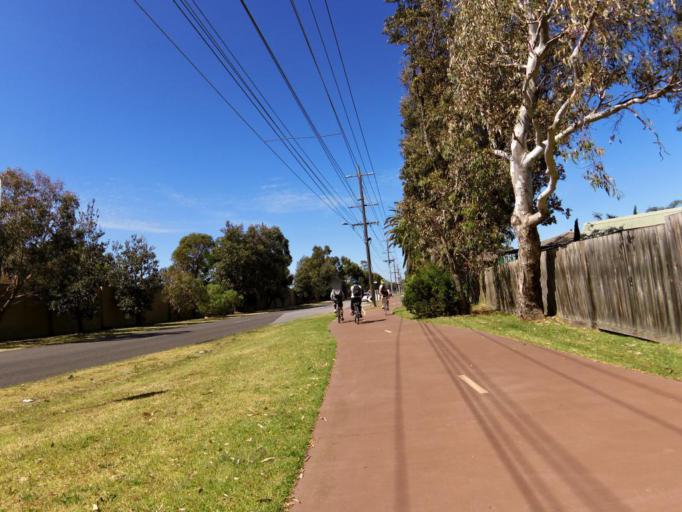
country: AU
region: Victoria
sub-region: Kingston
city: Patterson Lakes
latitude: -38.0769
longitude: 145.1490
